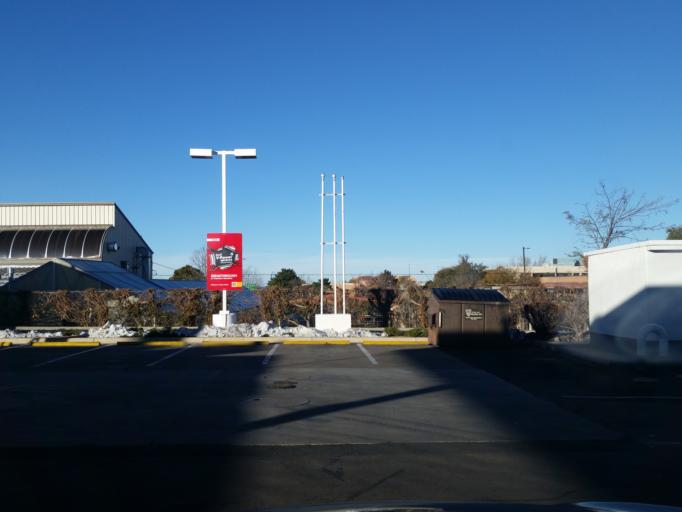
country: US
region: New Mexico
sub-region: Santa Fe County
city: Santa Fe
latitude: 35.6601
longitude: -105.9598
